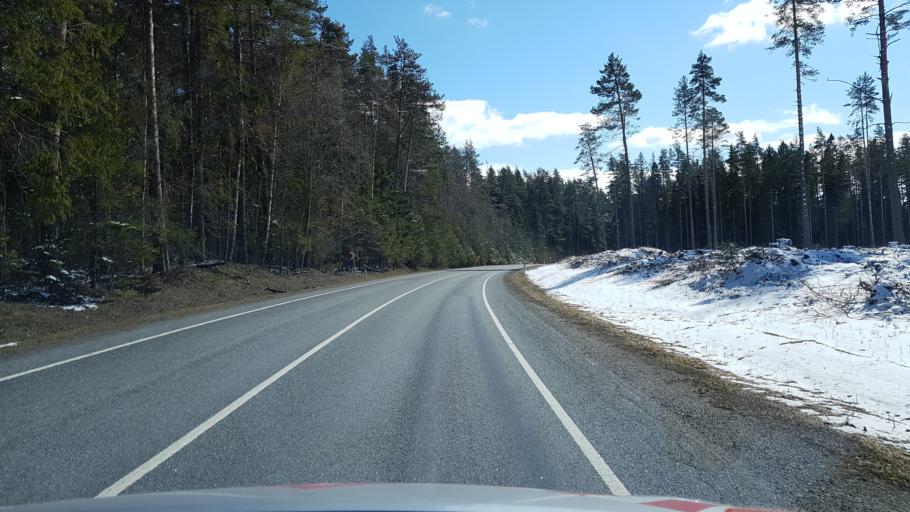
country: EE
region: Laeaene-Virumaa
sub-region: Tapa vald
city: Tapa
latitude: 59.4244
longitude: 25.9880
